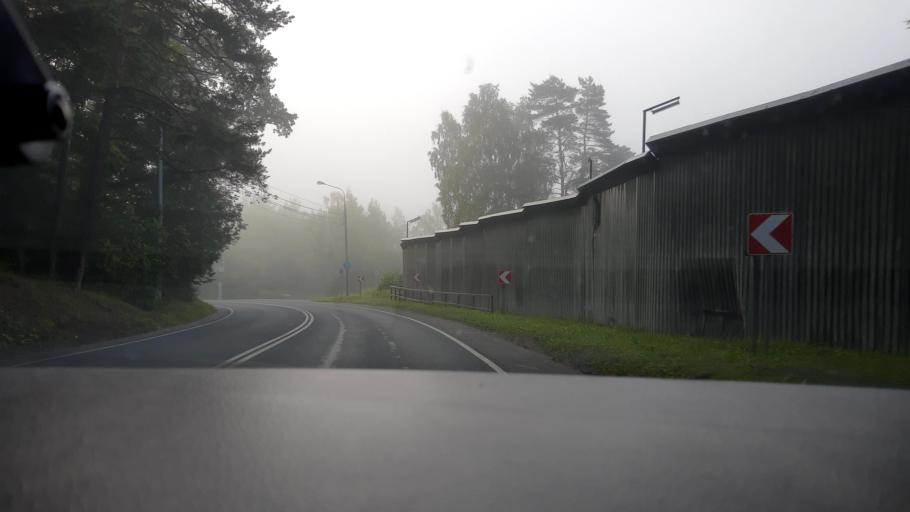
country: RU
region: Moskovskaya
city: Nikolina Gora
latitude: 55.7061
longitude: 37.0448
